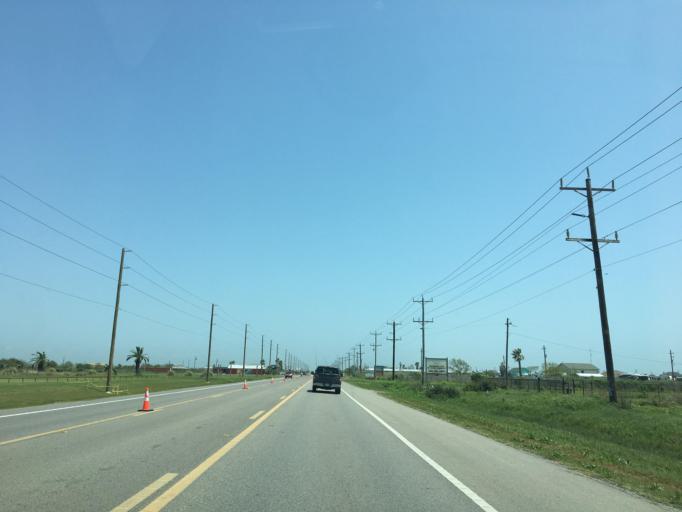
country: US
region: Texas
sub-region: Galveston County
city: Bolivar Peninsula
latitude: 29.4448
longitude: -94.6618
